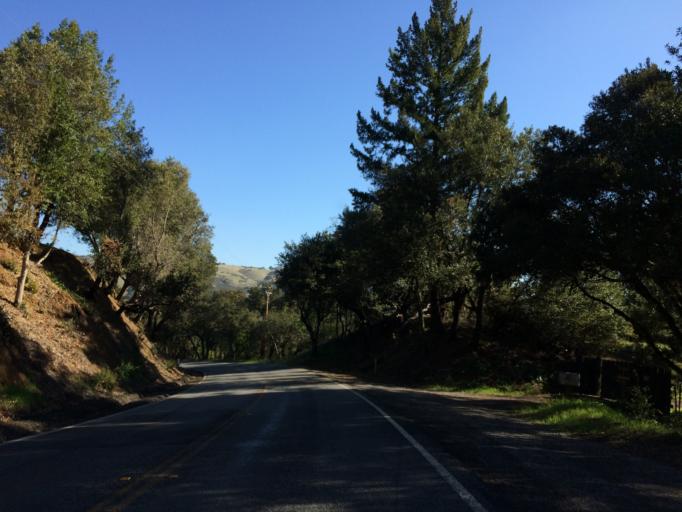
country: US
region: California
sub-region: Santa Clara County
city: Loyola
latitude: 37.3005
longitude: -122.1623
